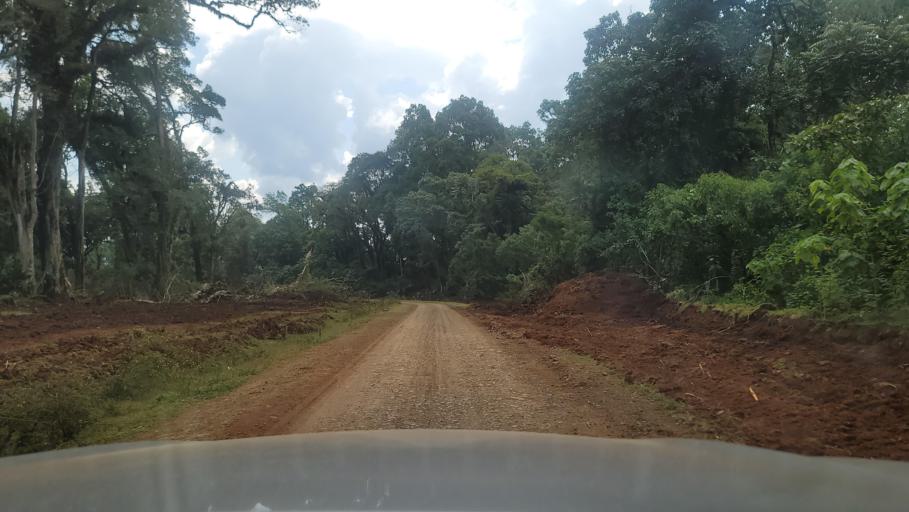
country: ET
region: Southern Nations, Nationalities, and People's Region
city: Bonga
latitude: 7.6649
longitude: 36.2430
